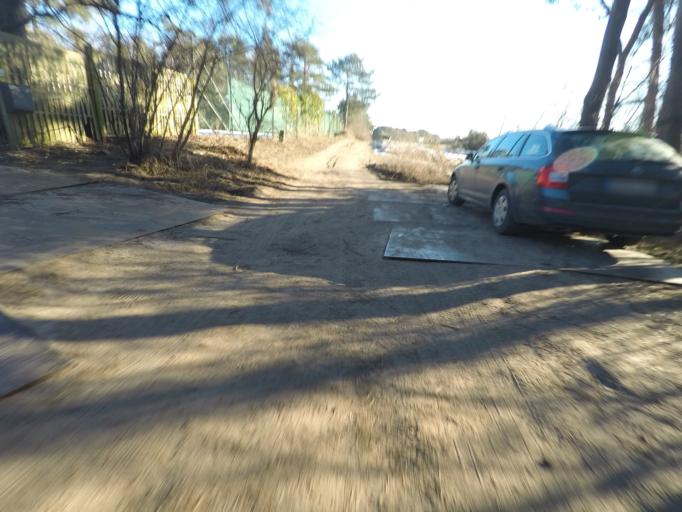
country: DK
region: Capital Region
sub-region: Halsnaes Kommune
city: Liseleje
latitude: 56.0031
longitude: 11.9381
